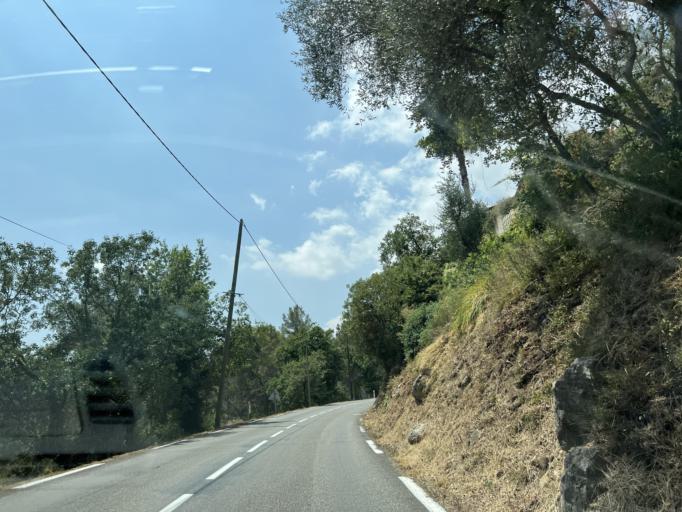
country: FR
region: Provence-Alpes-Cote d'Azur
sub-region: Departement des Alpes-Maritimes
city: Le Rouret
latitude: 43.7045
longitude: 7.0204
